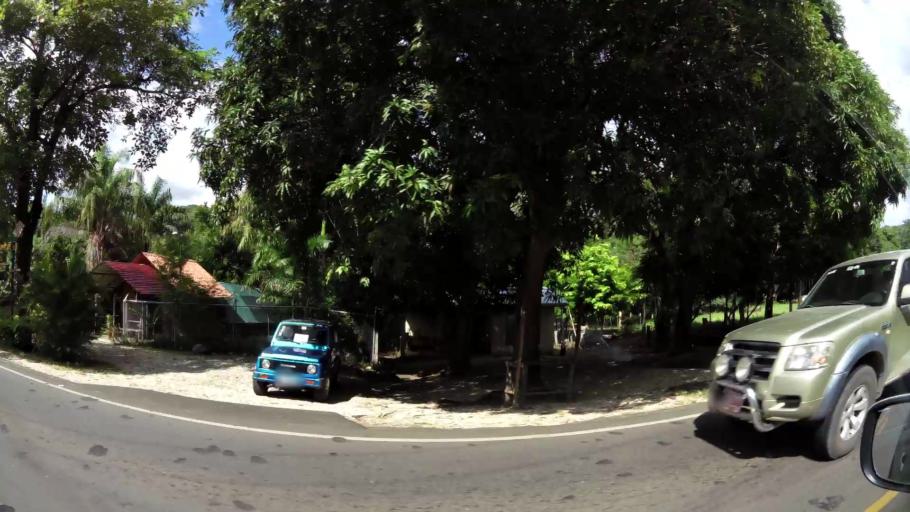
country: CR
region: Guanacaste
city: Hojancha
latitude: 10.1109
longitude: -85.3550
